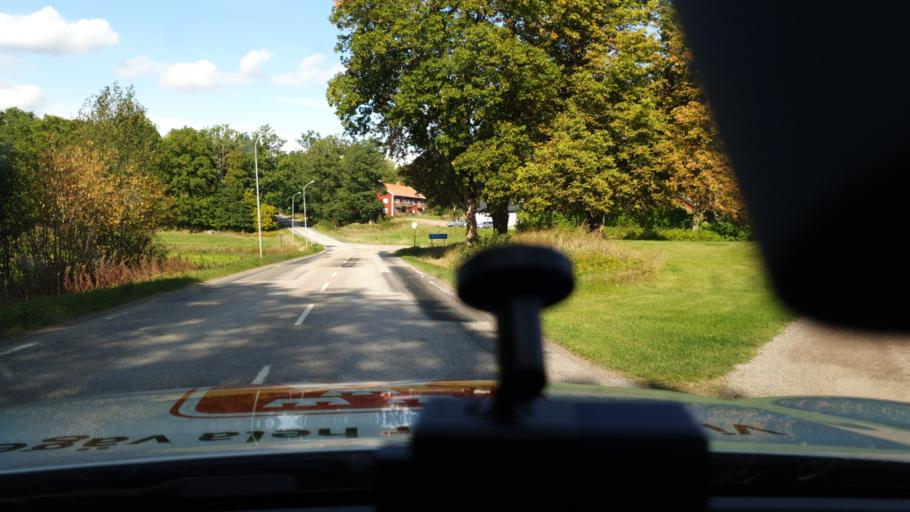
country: SE
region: Kalmar
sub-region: Vimmerby Kommun
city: Vimmerby
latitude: 57.7219
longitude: 16.0691
